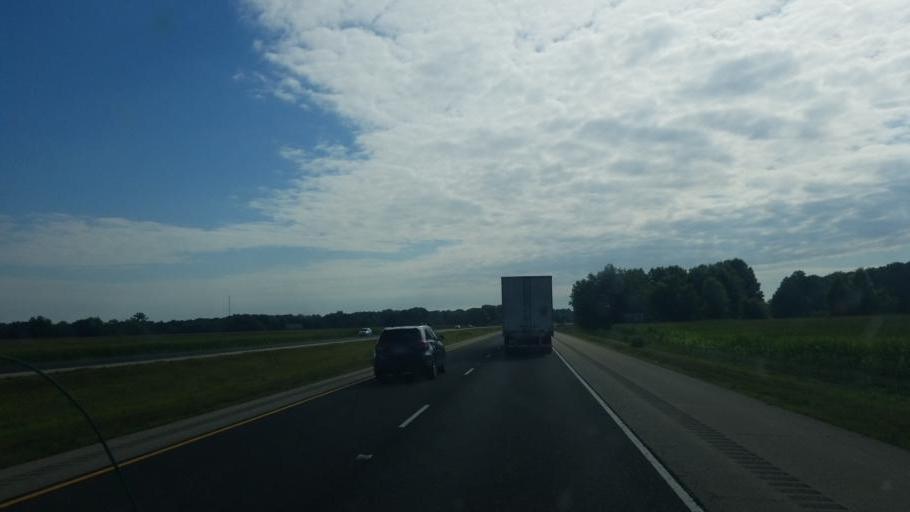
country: US
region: Illinois
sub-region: Clark County
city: Marshall
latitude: 39.4000
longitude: -87.7690
